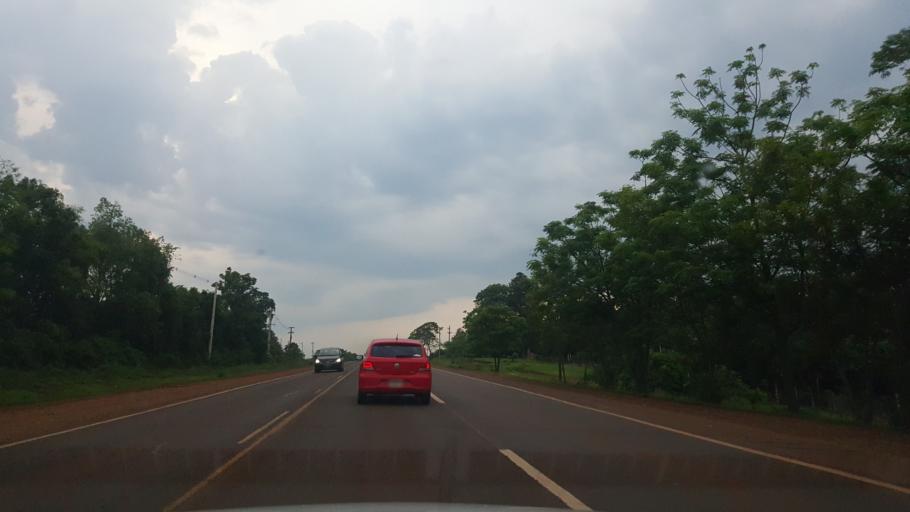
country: AR
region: Misiones
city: Santo Pipo
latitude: -27.1480
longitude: -55.4130
